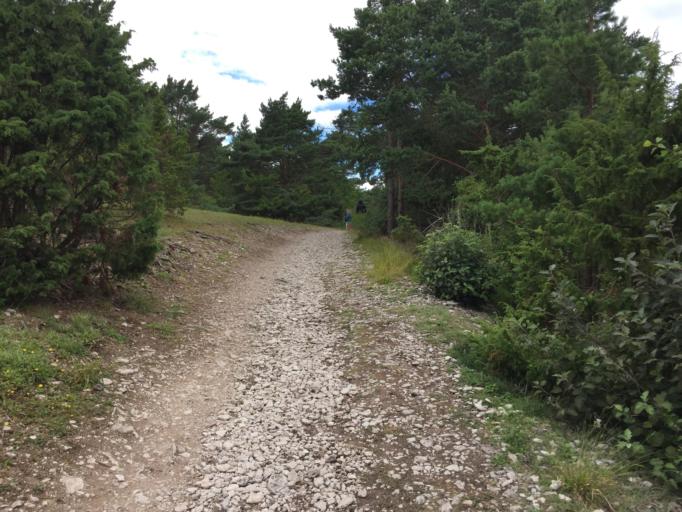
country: SE
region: Gotland
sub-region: Gotland
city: Visby
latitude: 57.8260
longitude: 18.5105
